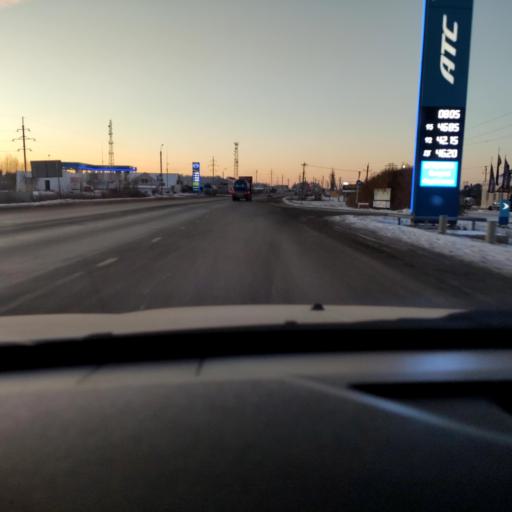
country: RU
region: Samara
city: Smyshlyayevka
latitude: 53.2562
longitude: 50.4755
